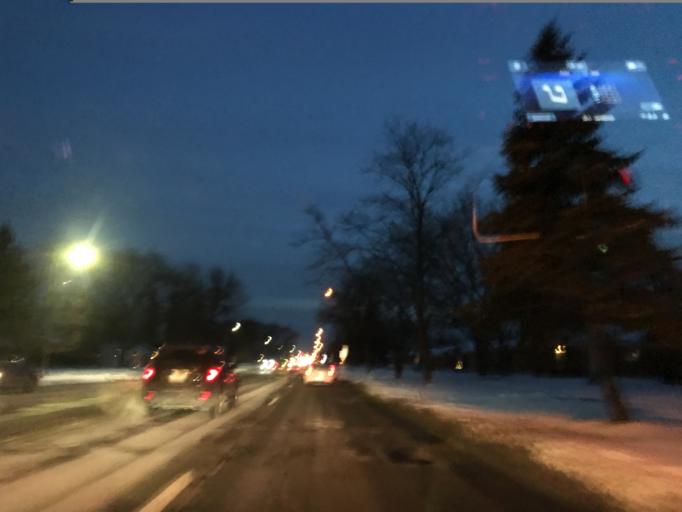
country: US
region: Michigan
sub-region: Wayne County
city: Redford
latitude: 42.3894
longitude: -83.3146
